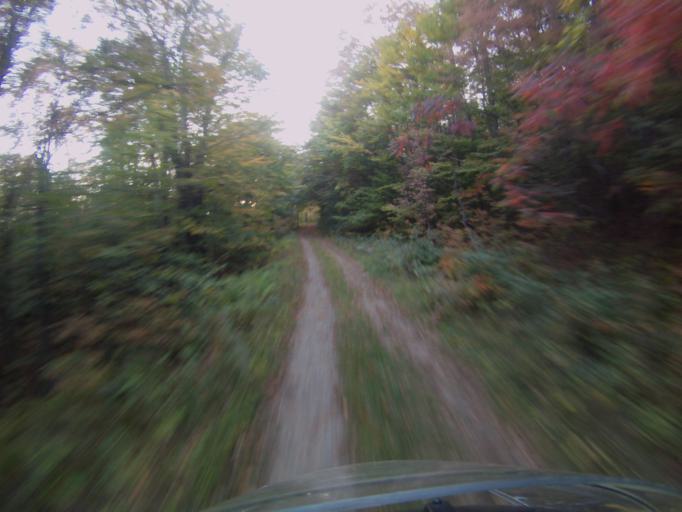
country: US
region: Vermont
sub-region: Addison County
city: Bristol
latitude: 44.0922
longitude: -72.9425
